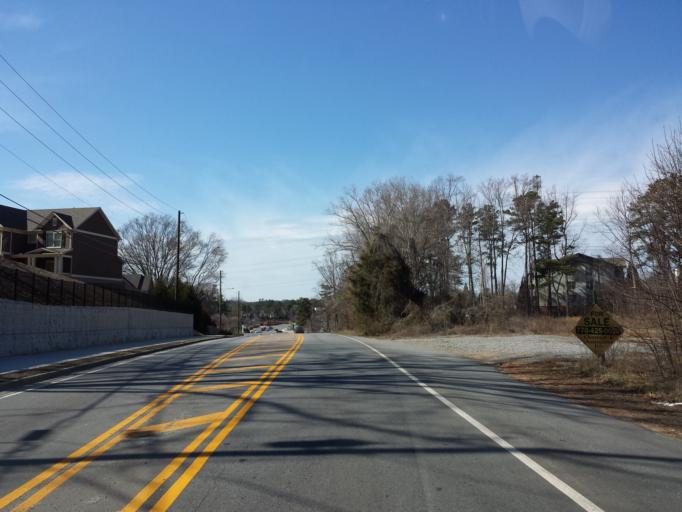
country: US
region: Georgia
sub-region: Cobb County
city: Kennesaw
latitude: 33.9904
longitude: -84.5940
